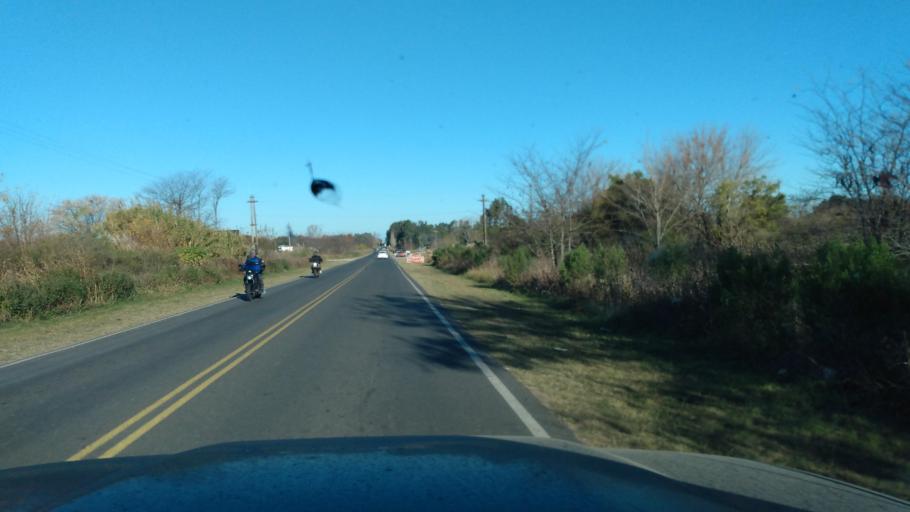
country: AR
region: Buenos Aires
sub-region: Partido de Lujan
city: Lujan
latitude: -34.5226
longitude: -59.1741
